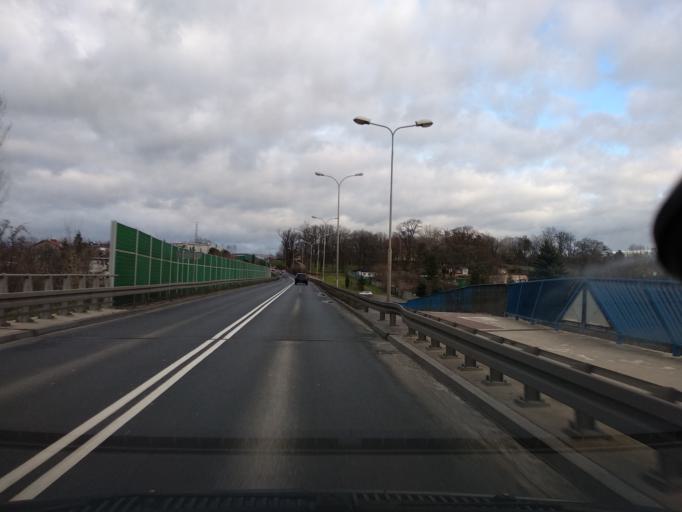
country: PL
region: Greater Poland Voivodeship
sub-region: Kalisz
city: Kalisz
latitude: 51.7733
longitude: 18.0747
